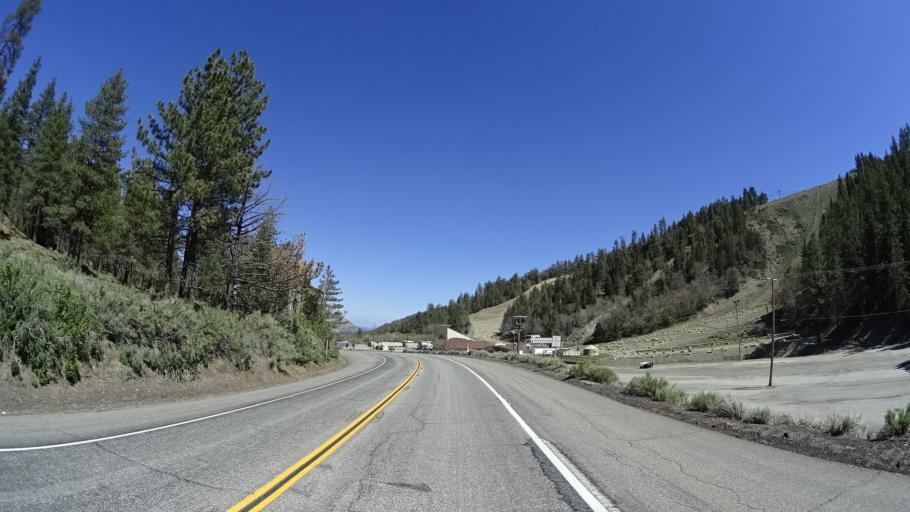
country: US
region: California
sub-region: San Bernardino County
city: Wrightwood
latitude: 34.3736
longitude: -117.6783
